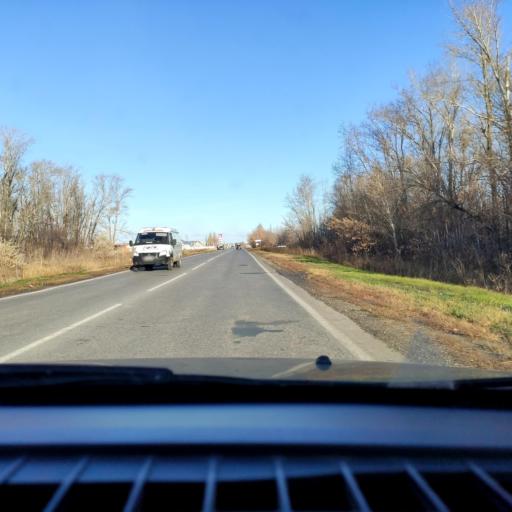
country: RU
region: Samara
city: Tol'yatti
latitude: 53.6305
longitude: 49.3031
